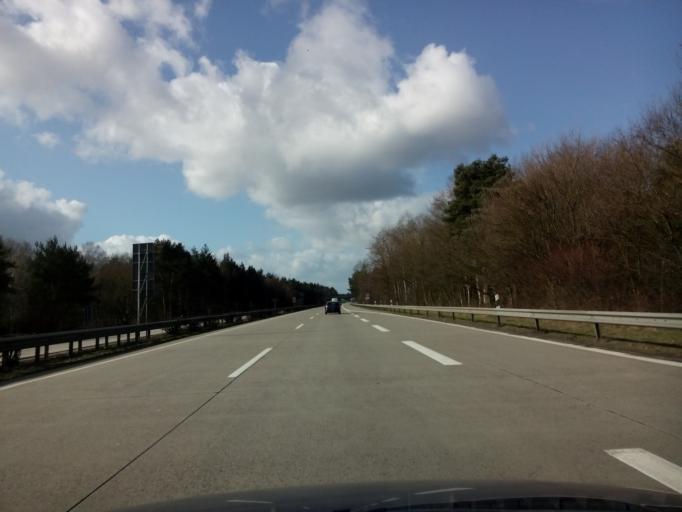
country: DE
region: Lower Saxony
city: Wildeshausen
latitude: 52.9153
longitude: 8.4467
